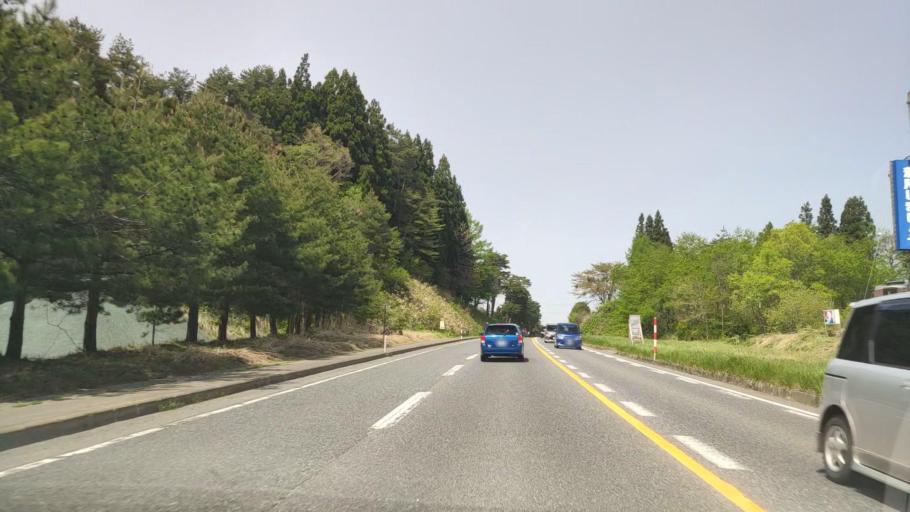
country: JP
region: Aomori
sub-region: Misawa Shi
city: Inuotose
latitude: 40.6661
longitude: 141.1861
